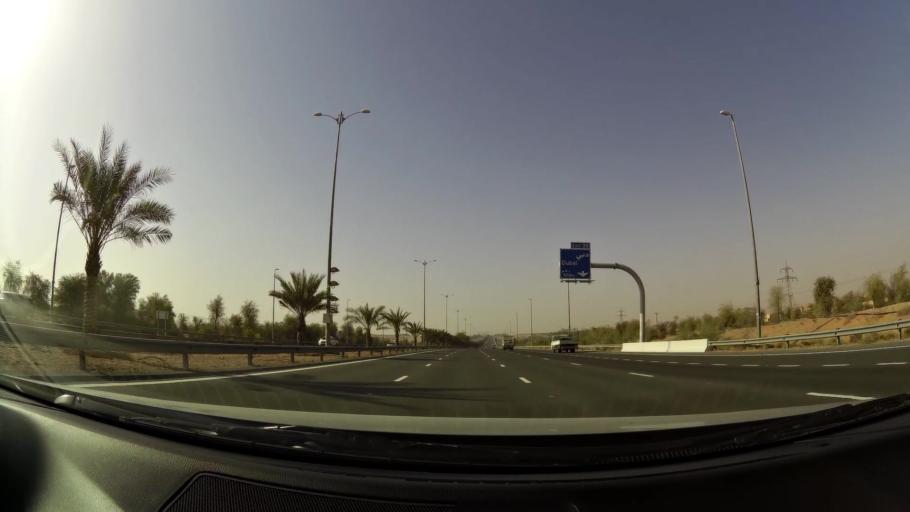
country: OM
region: Al Buraimi
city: Al Buraymi
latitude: 24.5571
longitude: 55.7531
